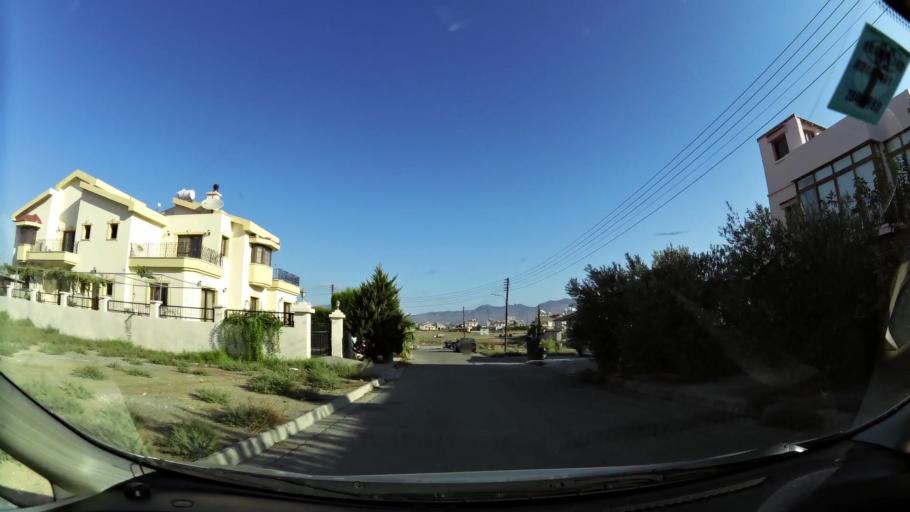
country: CY
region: Lefkosia
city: Nicosia
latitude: 35.2126
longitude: 33.2924
